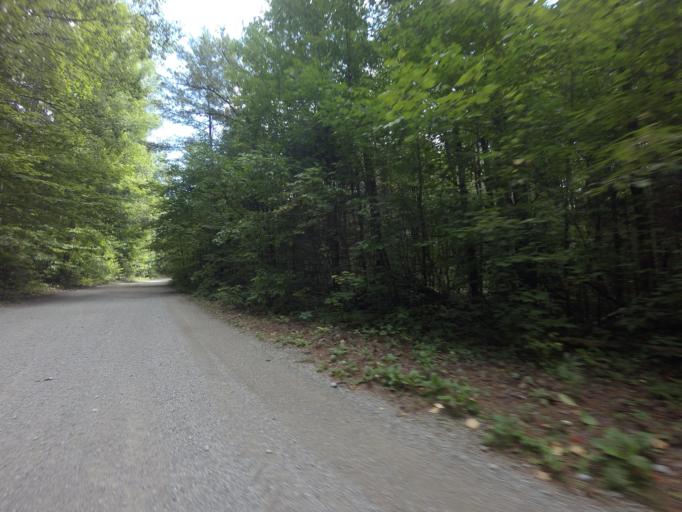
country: CA
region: Ontario
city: Omemee
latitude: 44.7610
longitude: -78.6727
